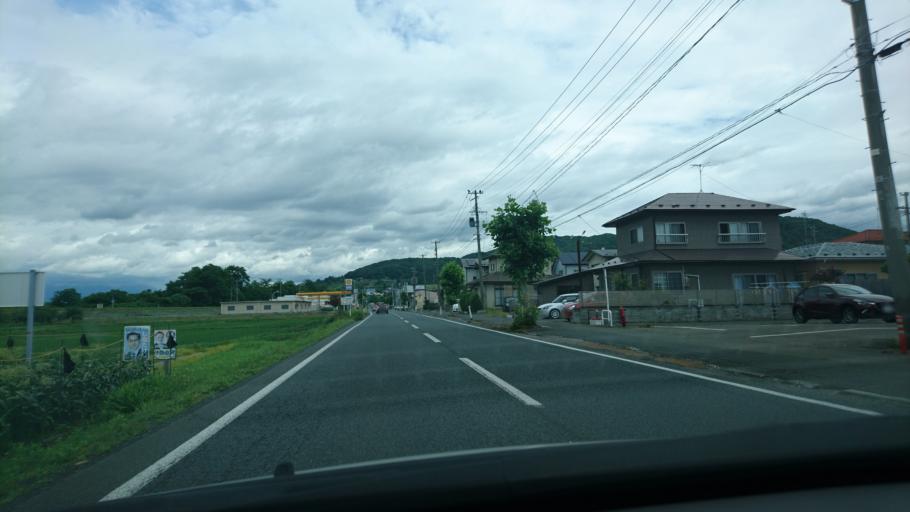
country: JP
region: Iwate
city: Morioka-shi
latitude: 39.6493
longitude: 141.1836
